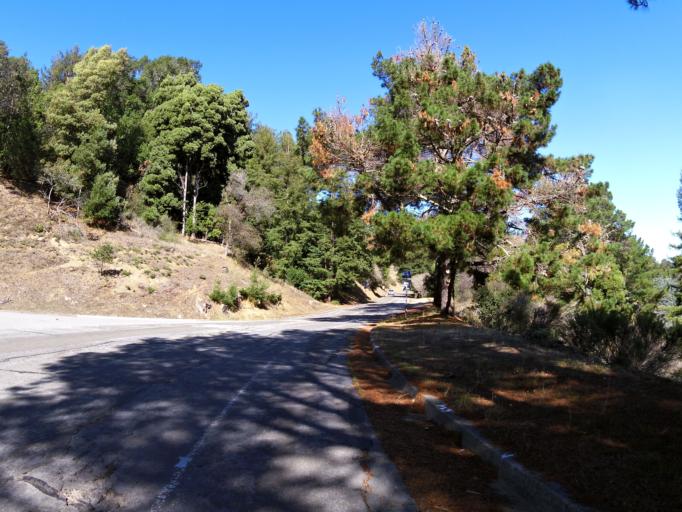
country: US
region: California
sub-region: Marin County
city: Mill Valley
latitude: 37.9086
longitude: -122.5283
